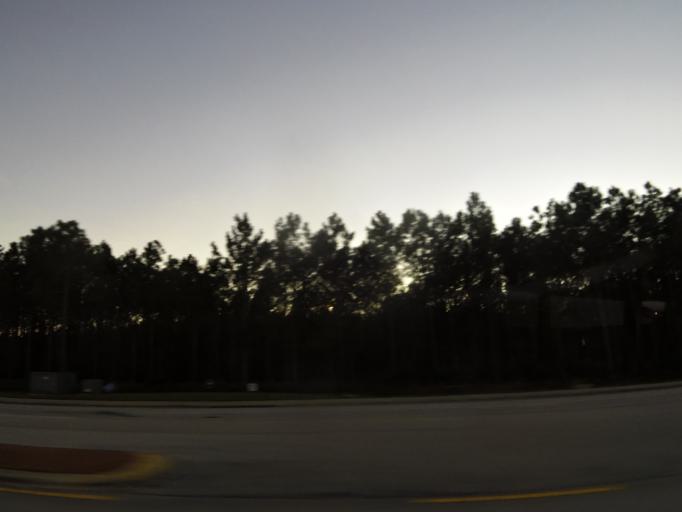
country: US
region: Florida
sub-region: Flagler County
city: Palm Coast
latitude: 29.5908
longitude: -81.2624
